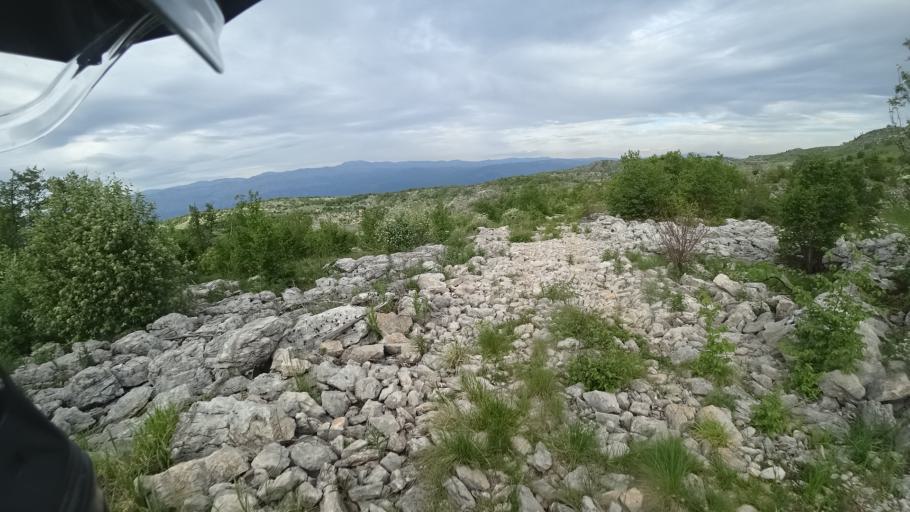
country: HR
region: Sibensko-Kniniska
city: Drnis
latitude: 43.8599
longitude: 16.3867
